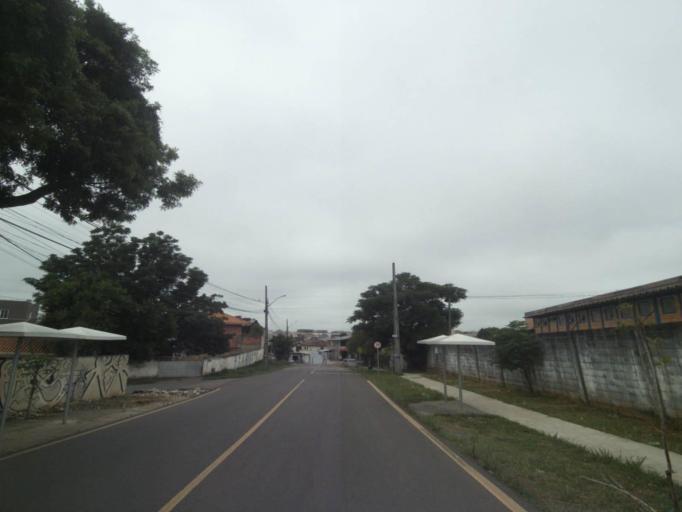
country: BR
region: Parana
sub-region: Curitiba
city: Curitiba
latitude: -25.4960
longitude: -49.3453
